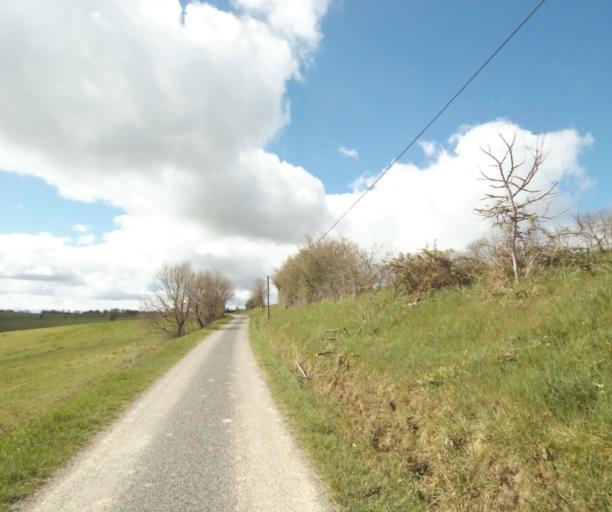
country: FR
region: Midi-Pyrenees
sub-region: Departement de l'Ariege
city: Saverdun
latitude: 43.1885
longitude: 1.5798
